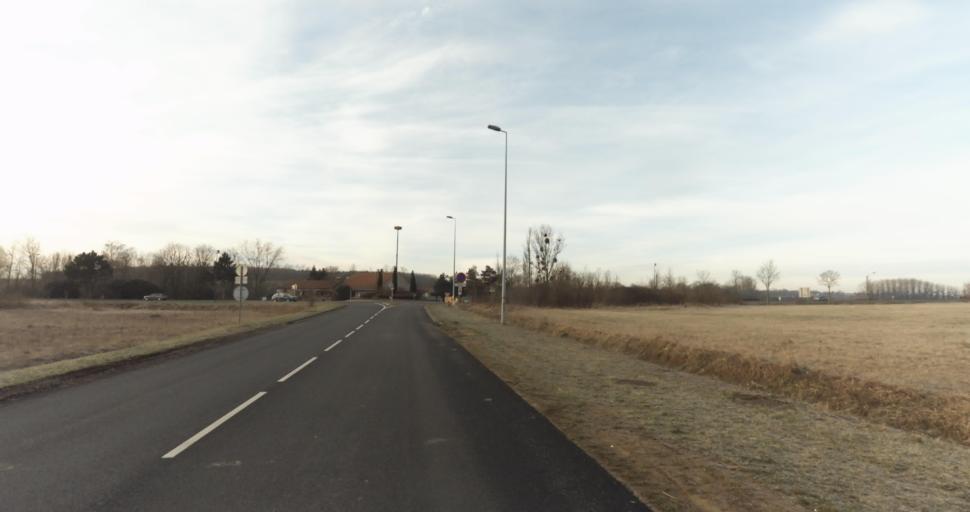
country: FR
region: Lorraine
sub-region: Departement de Meurthe-et-Moselle
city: Giraumont
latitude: 49.1527
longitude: 5.9031
